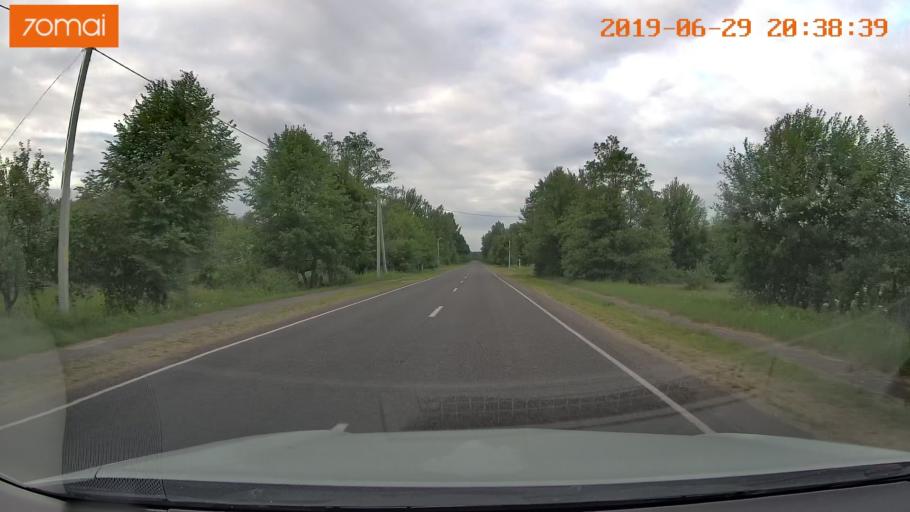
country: BY
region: Brest
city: Hantsavichy
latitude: 52.5525
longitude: 26.3643
